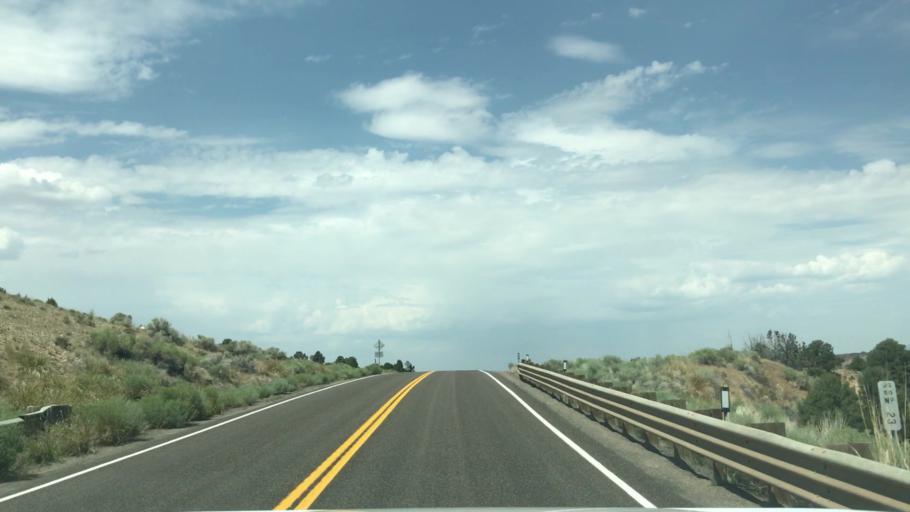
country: US
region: Nevada
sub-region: Eureka County
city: Eureka
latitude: 39.3912
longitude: -115.5036
